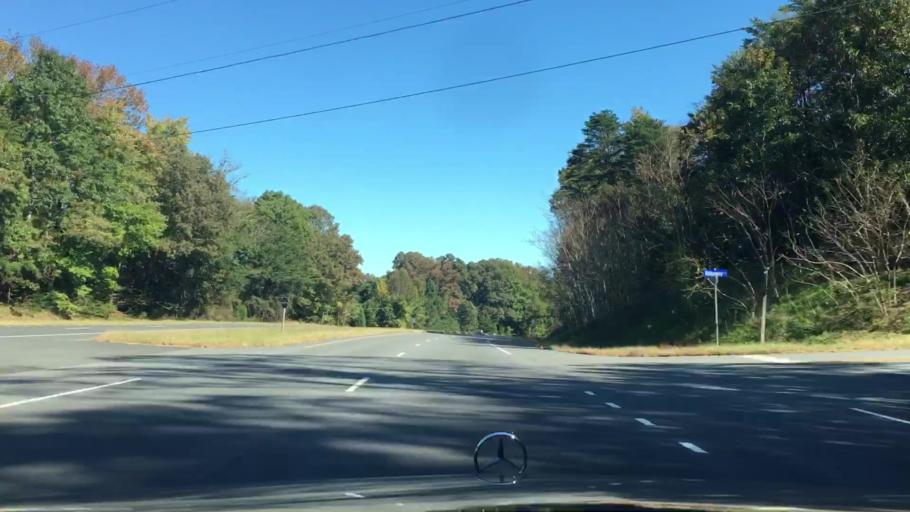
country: US
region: Virginia
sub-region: King George County
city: King George
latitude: 38.2768
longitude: -77.2315
